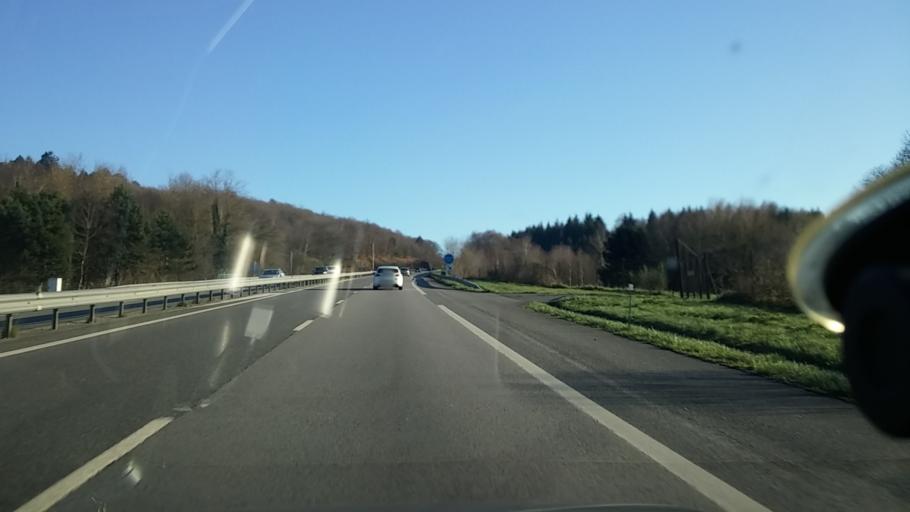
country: FR
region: Limousin
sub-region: Departement de la Haute-Vienne
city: Bessines-sur-Gartempe
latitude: 46.0699
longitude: 1.3604
